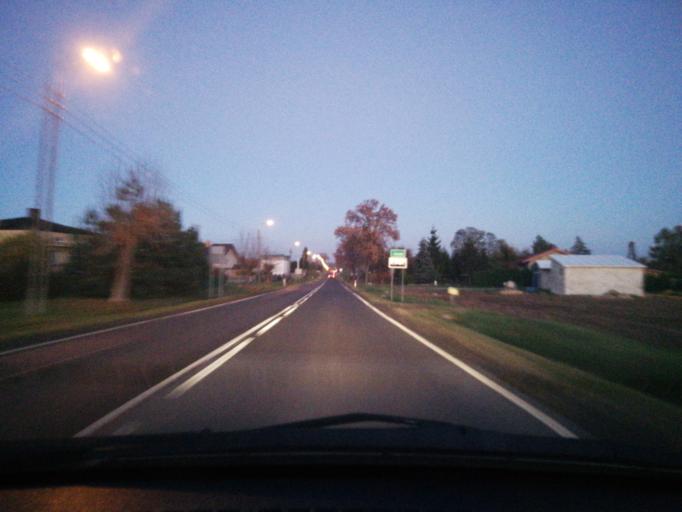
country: PL
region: Lodz Voivodeship
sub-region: Powiat brzezinski
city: Jezow
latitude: 51.8122
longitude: 19.9491
